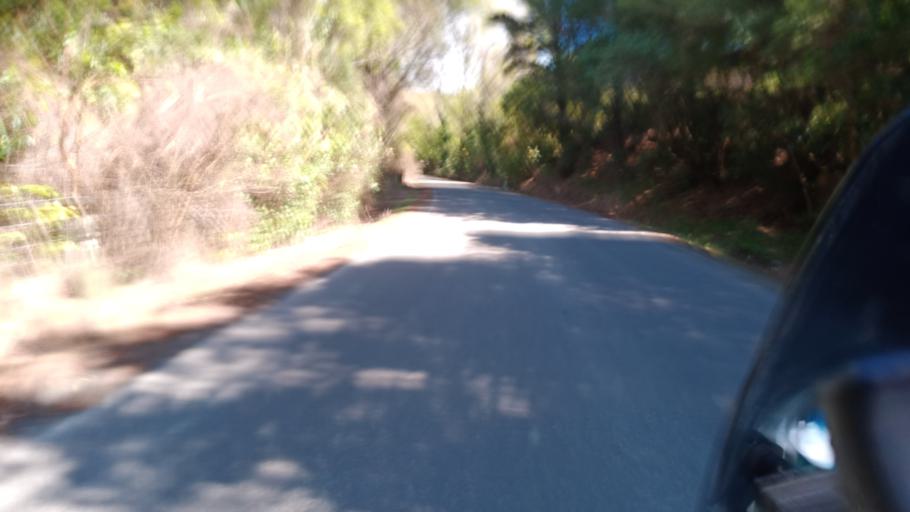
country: NZ
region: Gisborne
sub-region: Gisborne District
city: Gisborne
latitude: -38.7974
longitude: 177.7695
